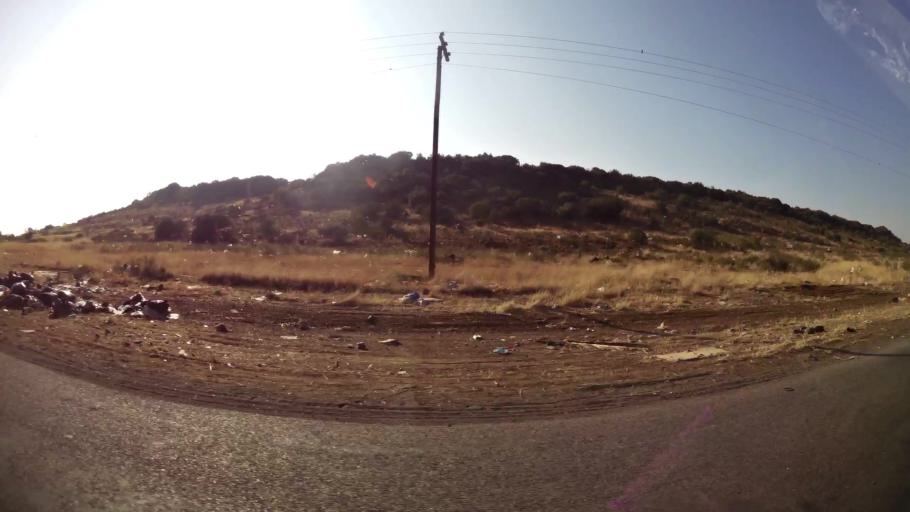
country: ZA
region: Orange Free State
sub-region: Mangaung Metropolitan Municipality
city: Bloemfontein
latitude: -29.1772
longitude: 26.1962
